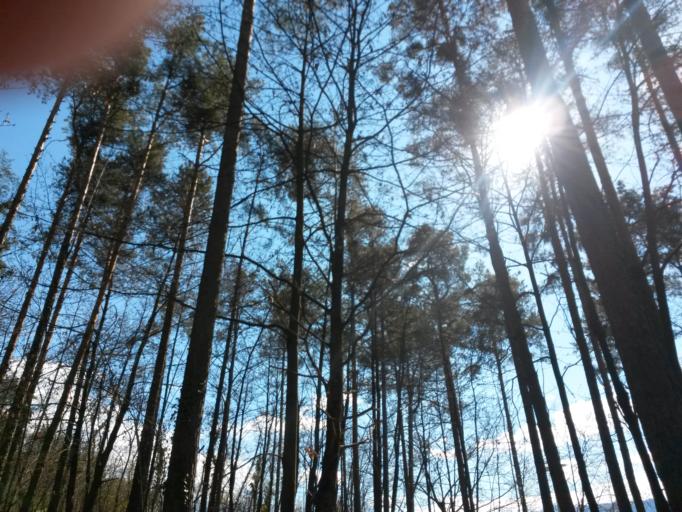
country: IT
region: Trentino-Alto Adige
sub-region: Bolzano
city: Cornaiano
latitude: 46.4468
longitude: 11.2903
